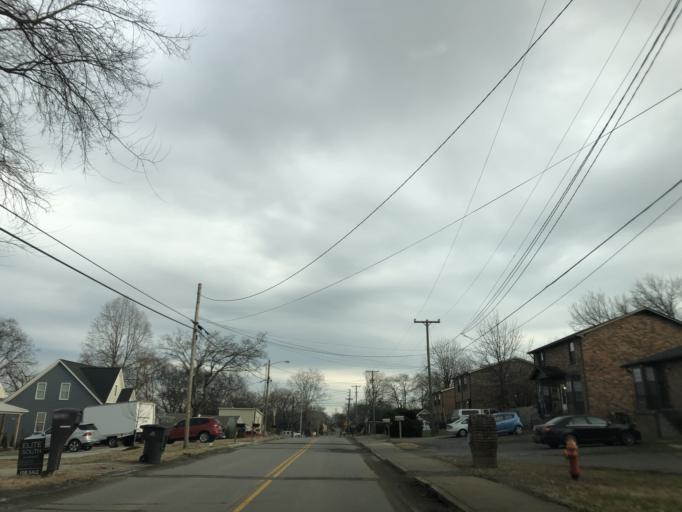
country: US
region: Tennessee
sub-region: Davidson County
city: Nashville
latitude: 36.2012
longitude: -86.7299
